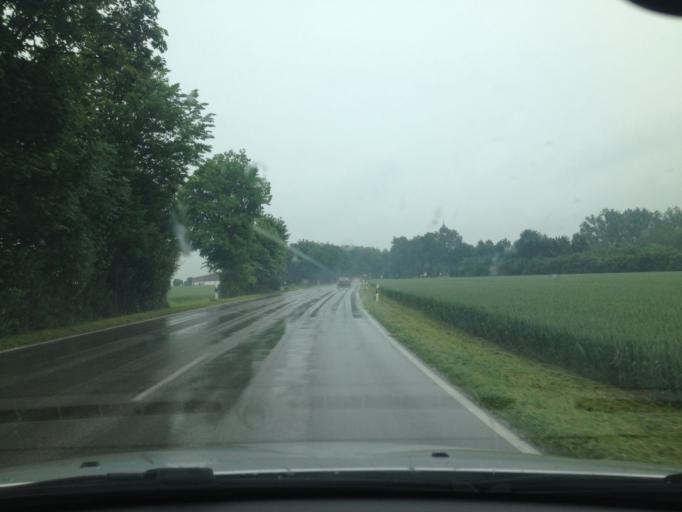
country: DE
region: Bavaria
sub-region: Swabia
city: Untermeitingen
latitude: 48.1643
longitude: 10.7997
